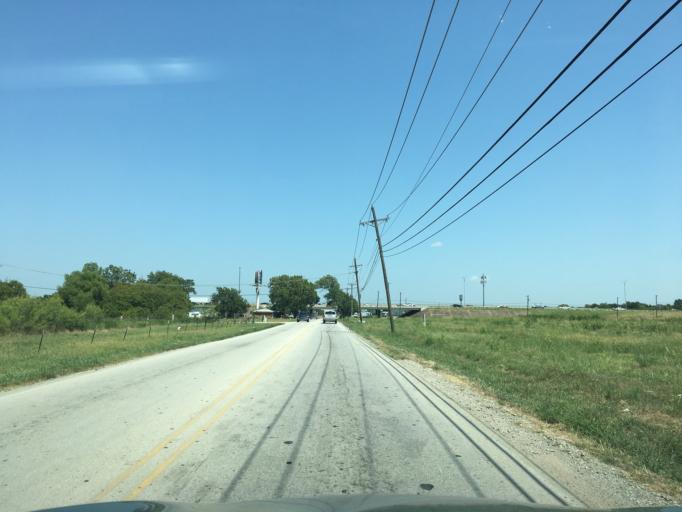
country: US
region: Texas
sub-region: Tarrant County
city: Everman
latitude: 32.6140
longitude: -97.3250
